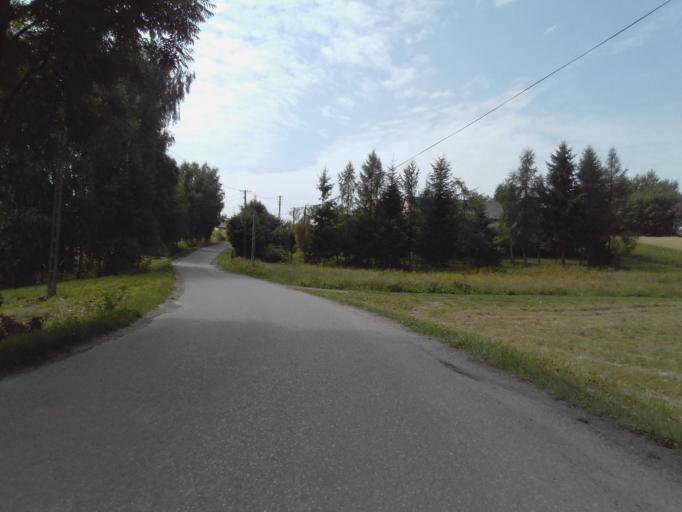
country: PL
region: Subcarpathian Voivodeship
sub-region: Powiat jasielski
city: Jaslo
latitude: 49.8055
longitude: 21.5059
